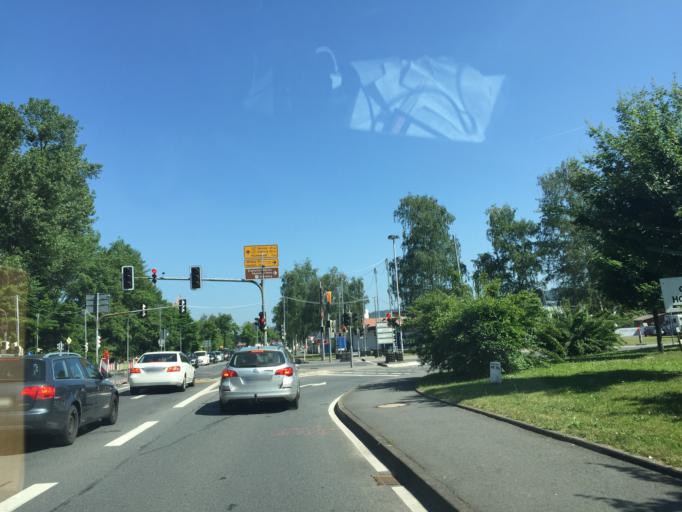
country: DE
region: Hesse
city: Michelstadt
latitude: 49.6707
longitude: 8.9992
